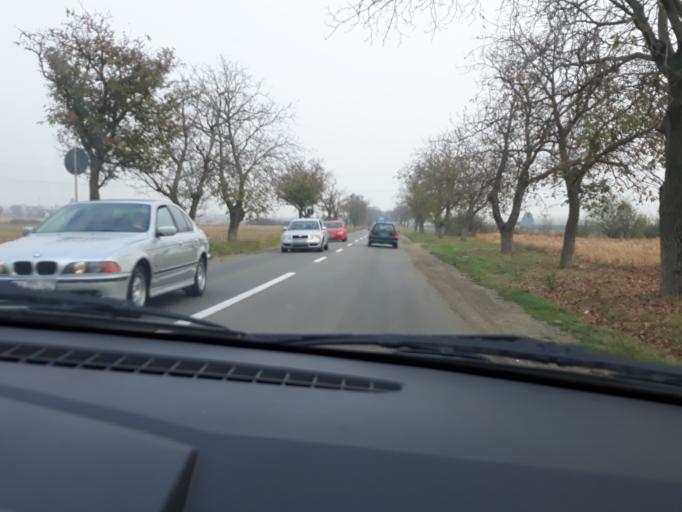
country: RO
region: Bihor
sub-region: Comuna Santandrei
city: Santandrei
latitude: 47.0540
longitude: 21.8709
